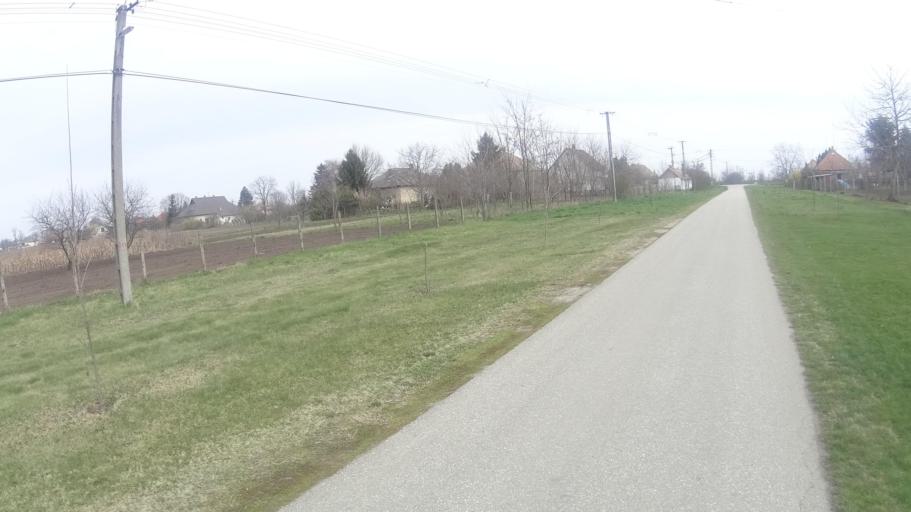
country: HU
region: Fejer
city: Sarosd
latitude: 46.9803
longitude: 18.6300
